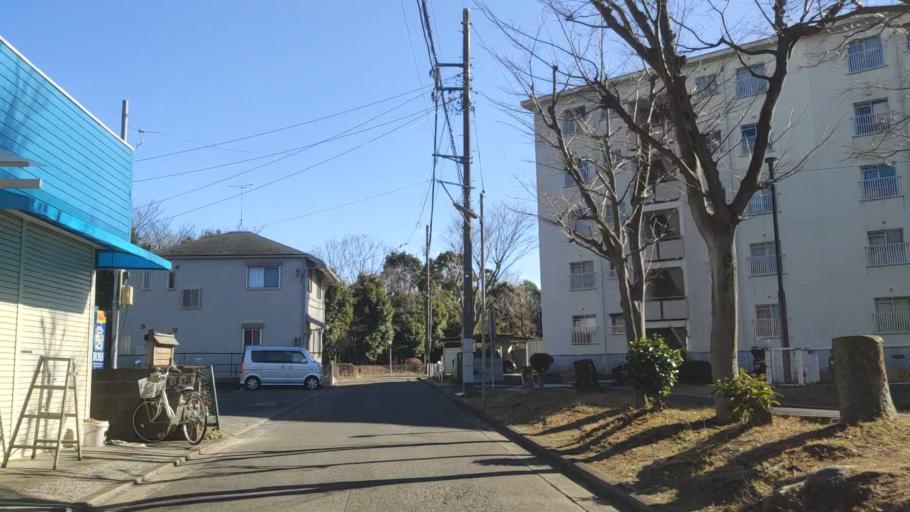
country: JP
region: Kanagawa
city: Minami-rinkan
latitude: 35.5027
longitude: 139.5309
